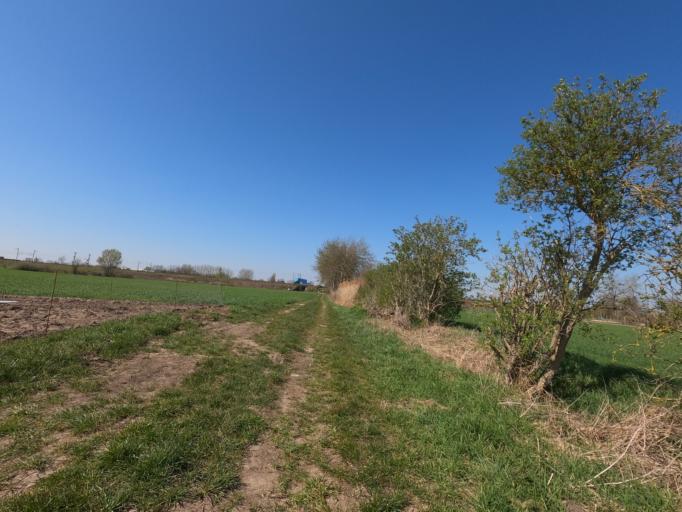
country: DE
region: Hesse
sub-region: Regierungsbezirk Darmstadt
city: Gross-Gerau
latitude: 49.9271
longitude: 8.5082
